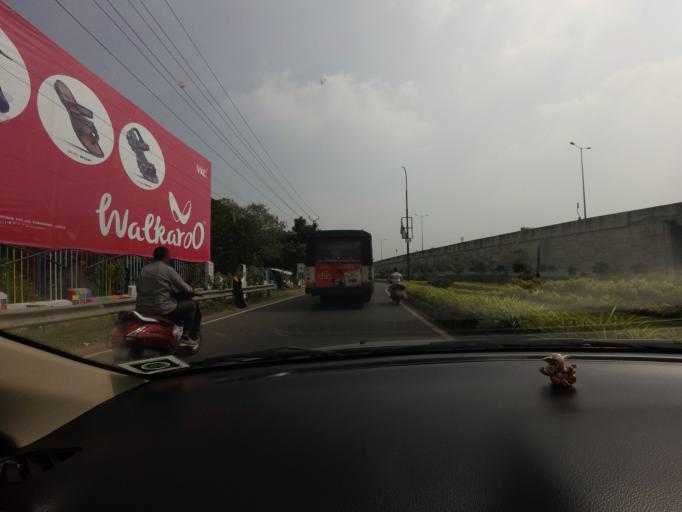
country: IN
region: Andhra Pradesh
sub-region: Krishna
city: Vijayawada
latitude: 16.5015
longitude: 80.6347
